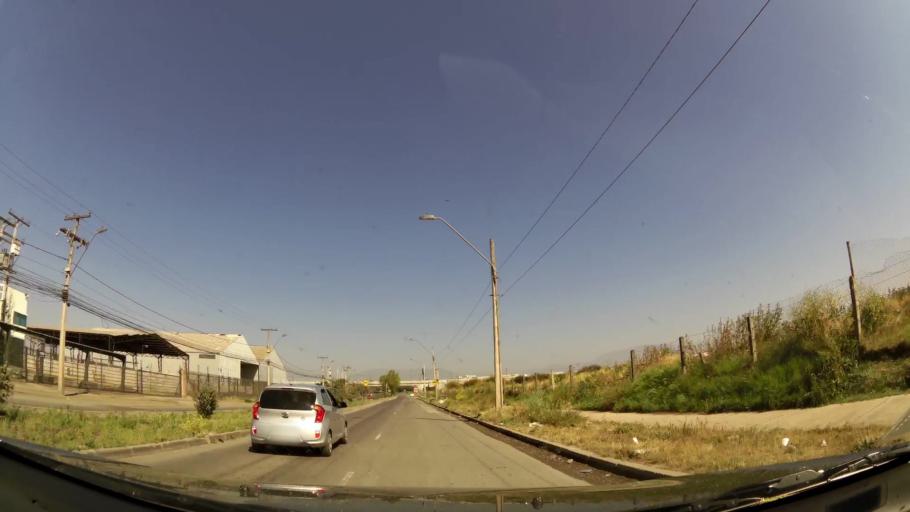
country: CL
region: Santiago Metropolitan
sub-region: Provincia de Chacabuco
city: Chicureo Abajo
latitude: -33.3249
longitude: -70.7154
